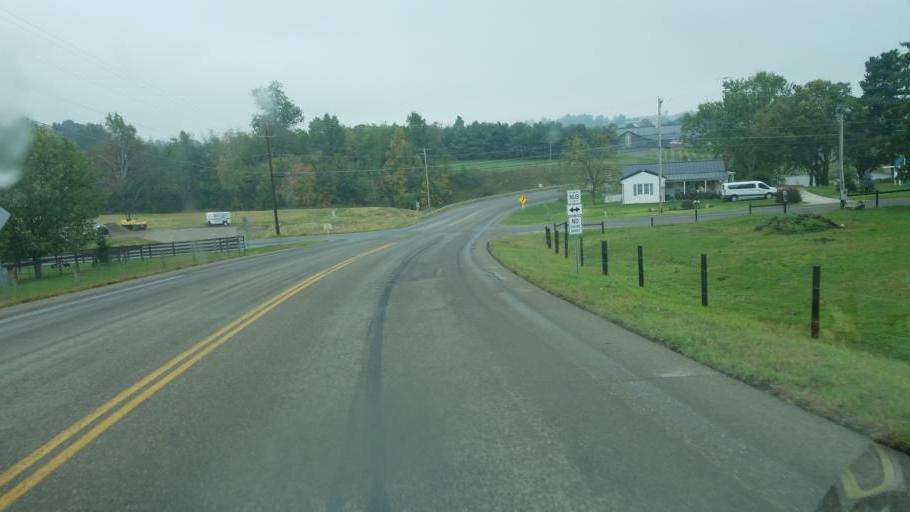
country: US
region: Ohio
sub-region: Holmes County
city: Millersburg
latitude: 40.5721
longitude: -81.7805
